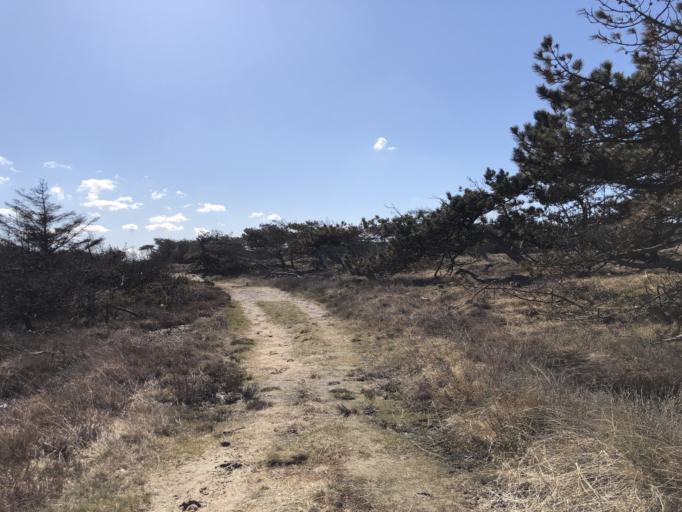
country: DK
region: Central Jutland
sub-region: Holstebro Kommune
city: Ulfborg
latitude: 56.3056
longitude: 8.1299
